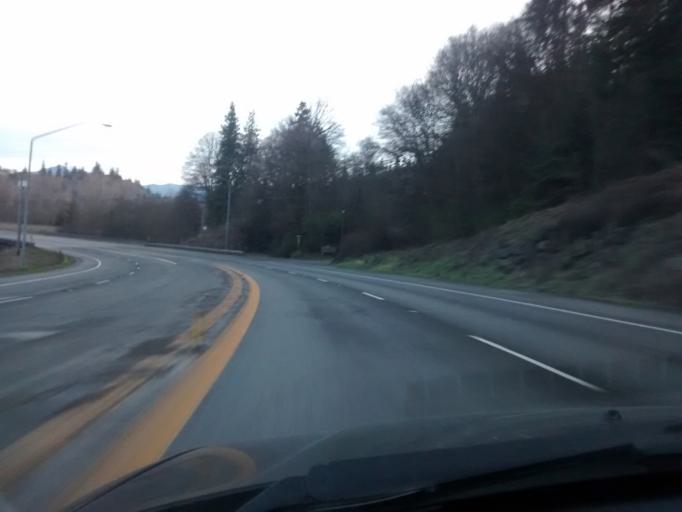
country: US
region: Washington
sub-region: Clallam County
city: Port Angeles East
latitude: 48.1049
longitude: -123.3581
